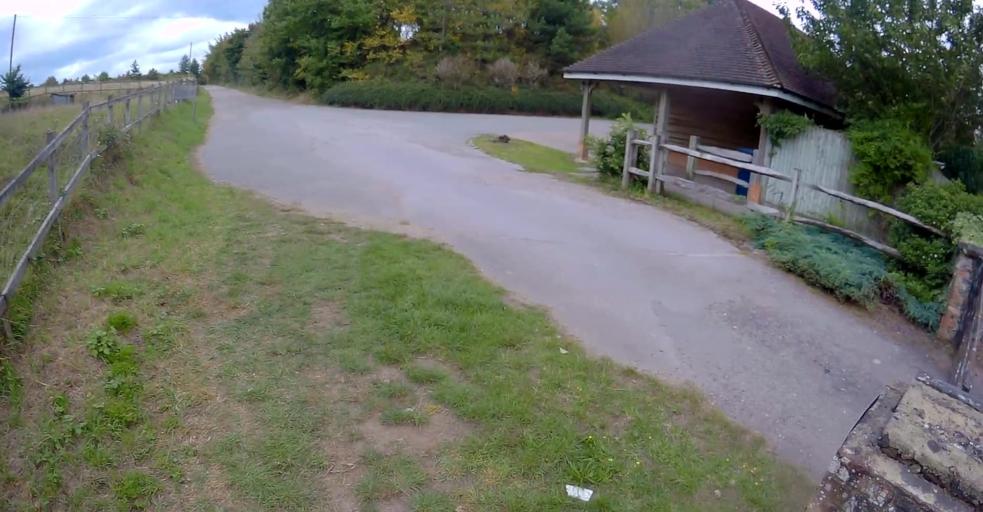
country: GB
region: England
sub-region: Surrey
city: Hale
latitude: 51.2189
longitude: -0.7706
